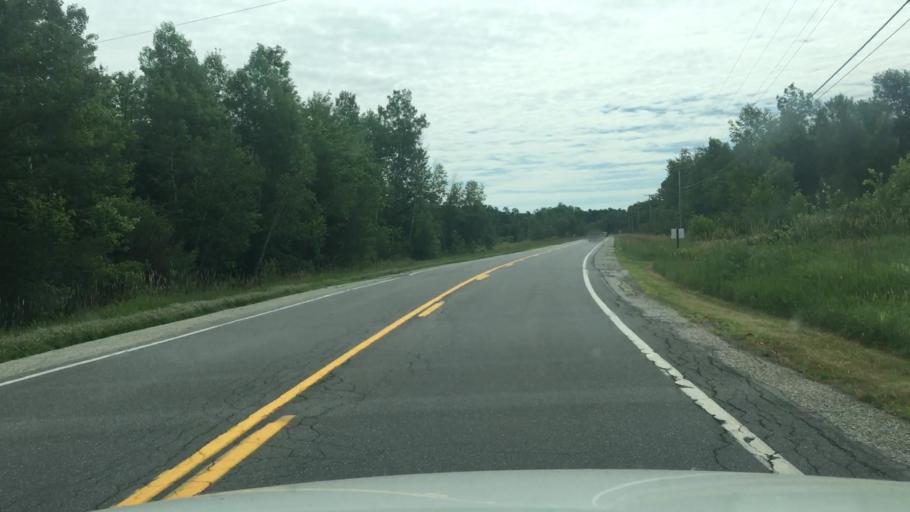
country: US
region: Maine
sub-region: Waldo County
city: Burnham
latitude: 44.6185
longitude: -69.3886
